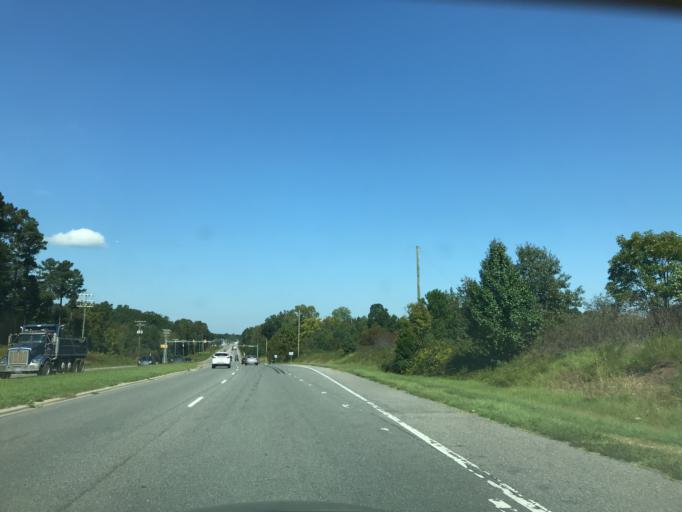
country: US
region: North Carolina
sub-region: Wake County
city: Morrisville
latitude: 35.8781
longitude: -78.8916
